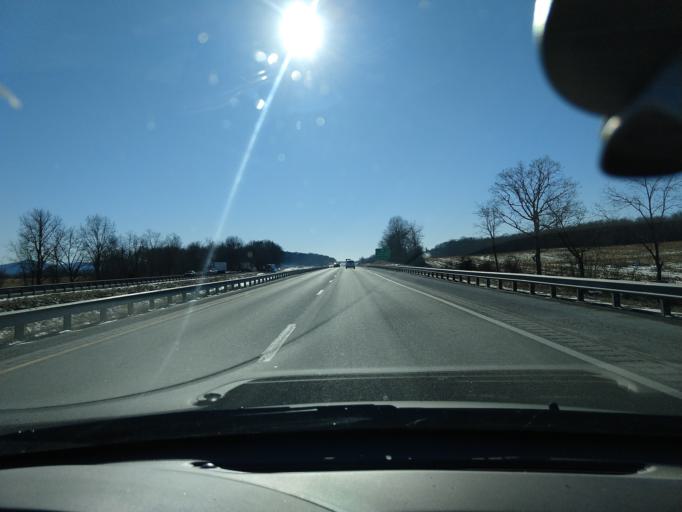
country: US
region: Virginia
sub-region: Augusta County
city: Stuarts Draft
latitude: 37.9475
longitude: -79.2141
